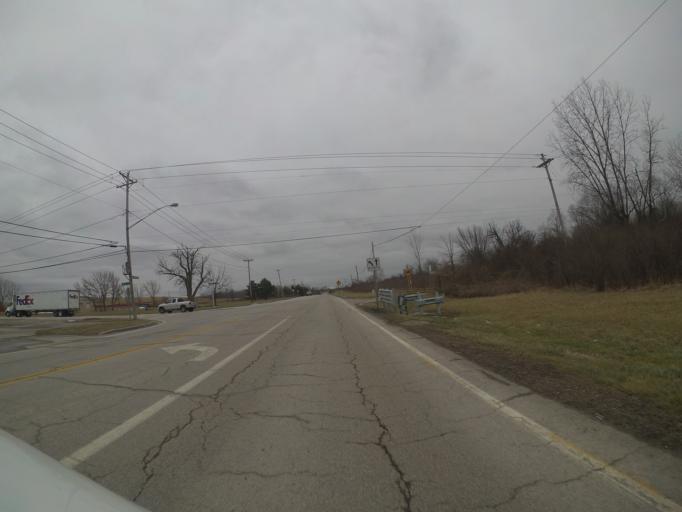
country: US
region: Ohio
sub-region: Wood County
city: Walbridge
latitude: 41.6089
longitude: -83.5124
